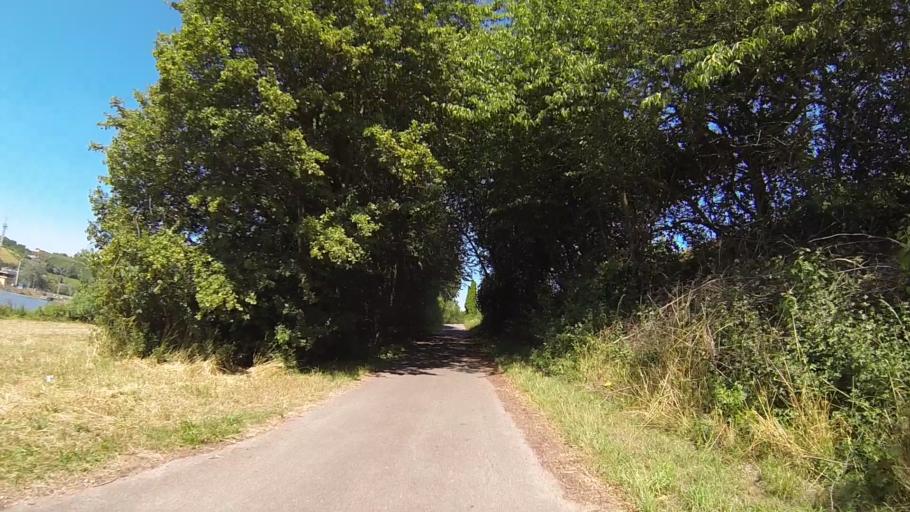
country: DE
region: Rheinland-Pfalz
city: Palzem
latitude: 49.5675
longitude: 6.3671
